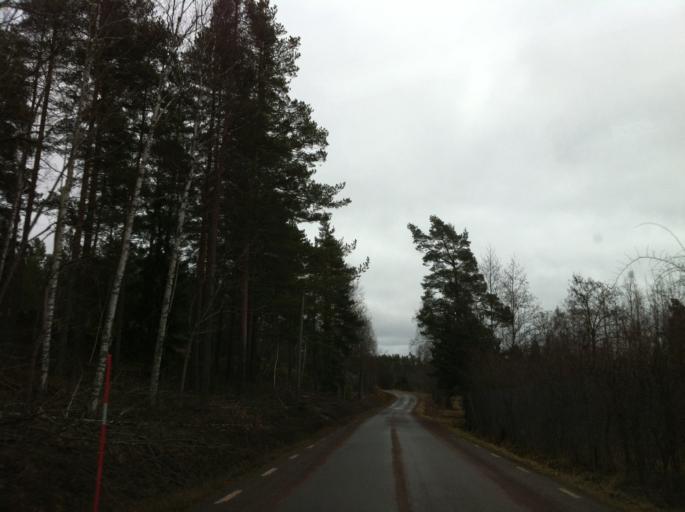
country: SE
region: Kalmar
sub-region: Vasterviks Kommun
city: Forserum
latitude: 57.9255
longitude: 16.5501
